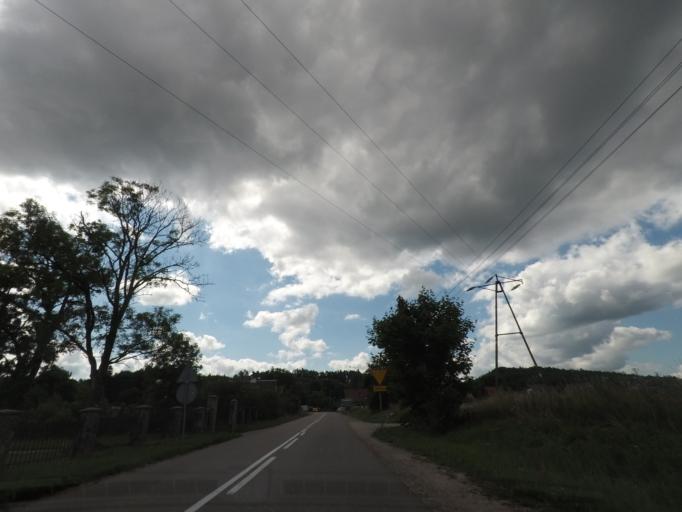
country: PL
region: Pomeranian Voivodeship
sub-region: Powiat wejherowski
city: Leczyce
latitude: 54.5754
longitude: 17.8654
